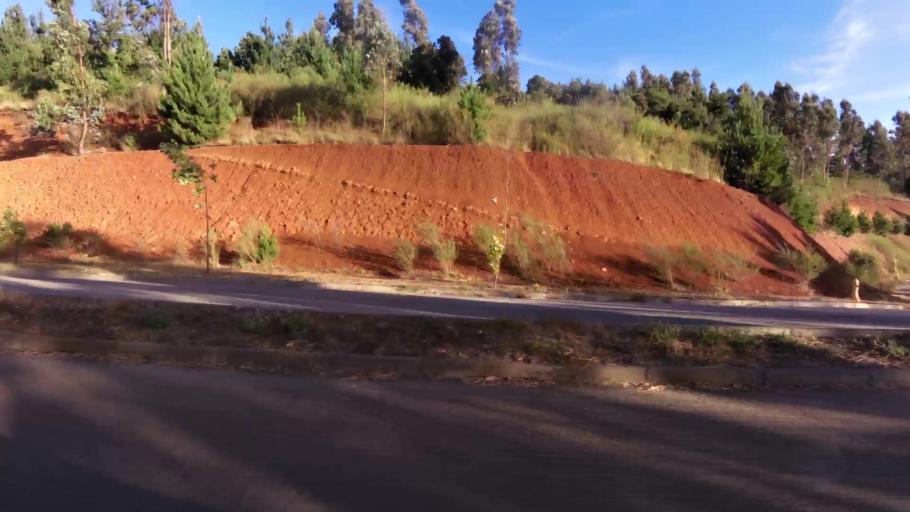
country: CL
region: Biobio
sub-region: Provincia de Concepcion
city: Concepcion
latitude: -36.8603
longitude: -73.0940
